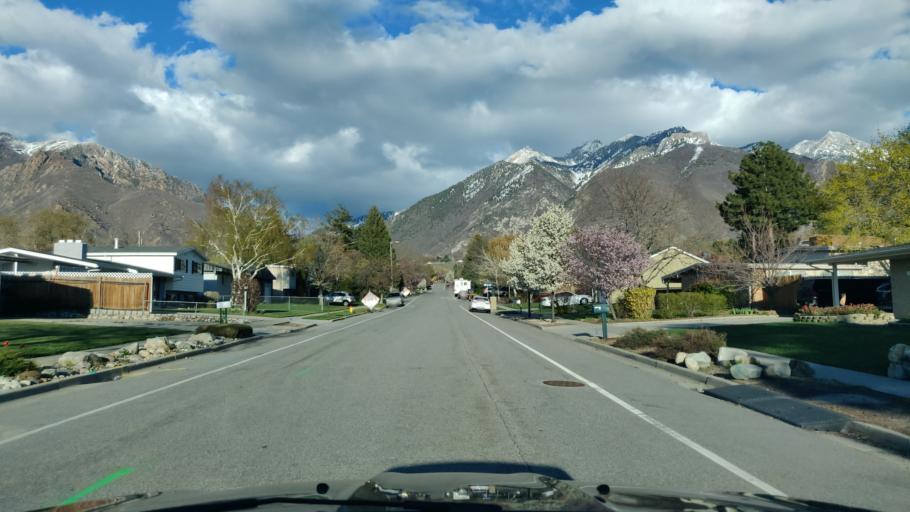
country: US
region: Utah
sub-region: Salt Lake County
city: Cottonwood Heights
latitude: 40.6163
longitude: -111.8129
